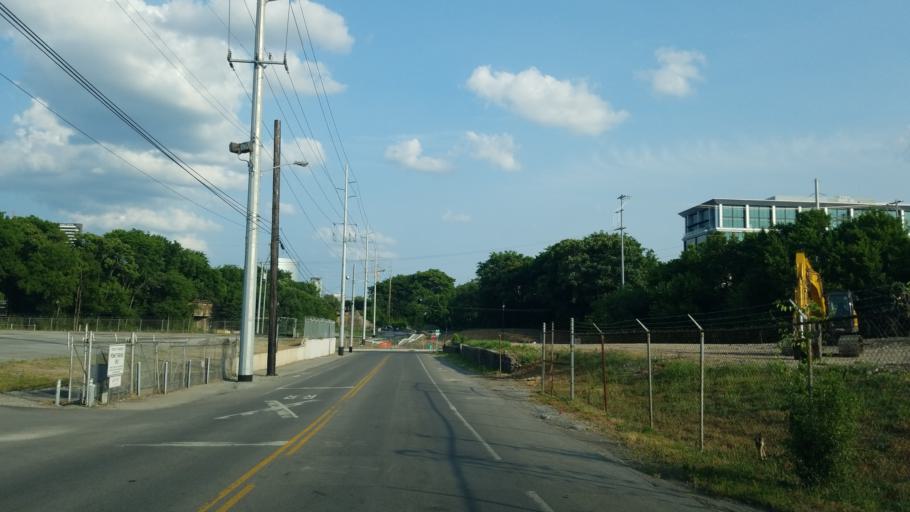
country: US
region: Tennessee
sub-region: Davidson County
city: Nashville
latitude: 36.1666
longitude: -86.7909
